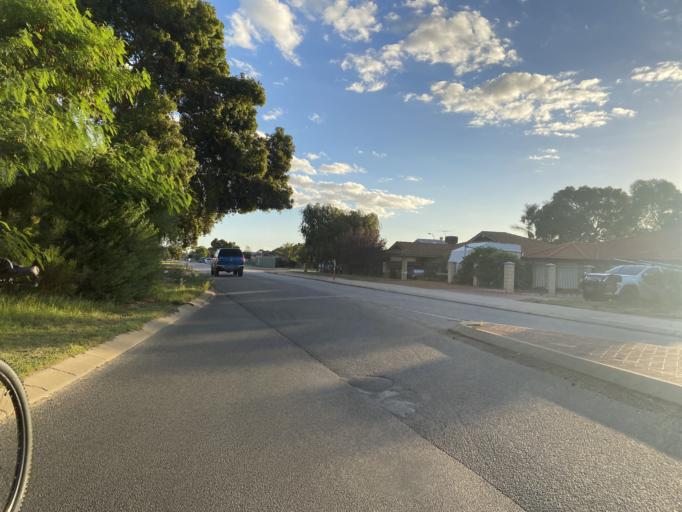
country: AU
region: Western Australia
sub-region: Kalamunda
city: Maida Vale
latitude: -31.9695
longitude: 116.0067
